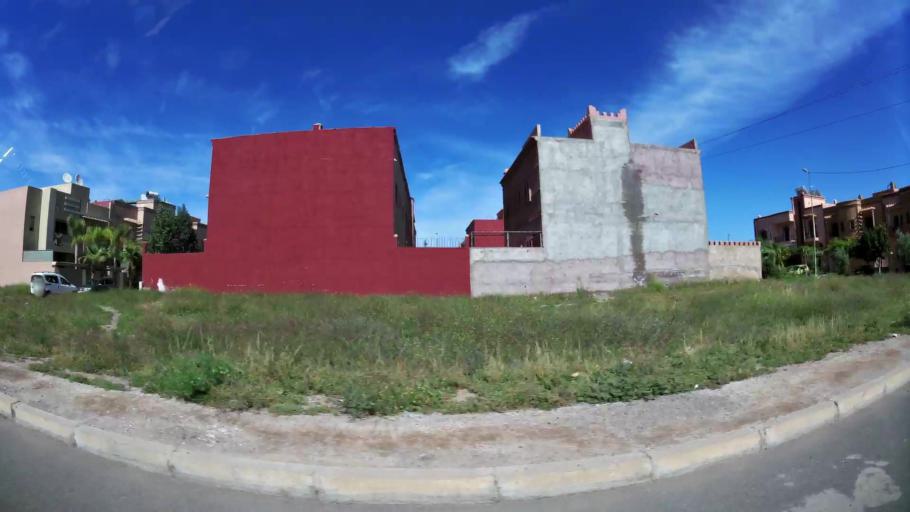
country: MA
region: Marrakech-Tensift-Al Haouz
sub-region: Marrakech
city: Marrakesh
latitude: 31.6424
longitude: -8.0437
